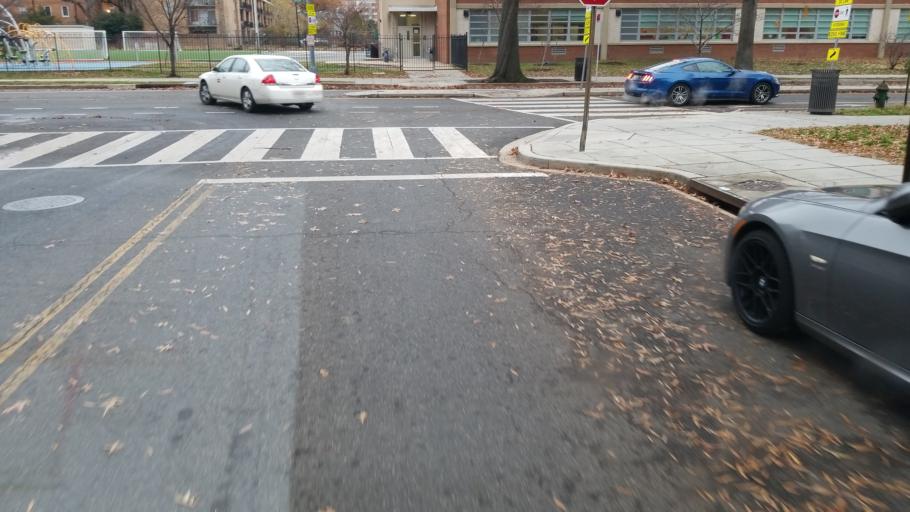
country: US
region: Washington, D.C.
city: Washington, D.C.
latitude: 38.8791
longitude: -77.0188
